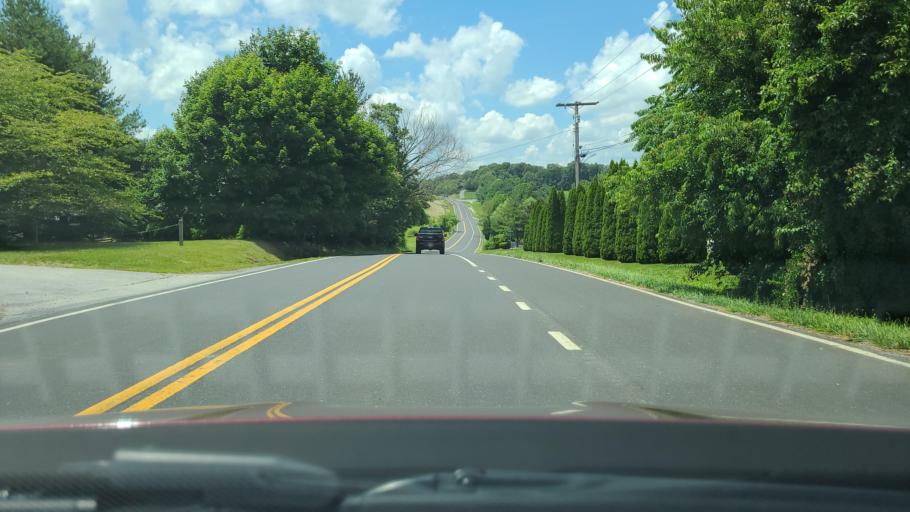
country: US
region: Maryland
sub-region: Carroll County
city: Westminster
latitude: 39.5392
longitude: -77.0022
